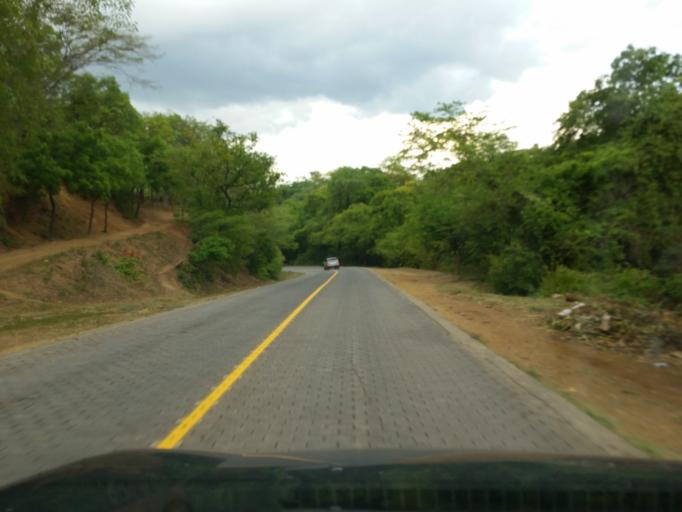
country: NI
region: Managua
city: Carlos Fonseca Amador
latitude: 11.9004
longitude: -86.5114
